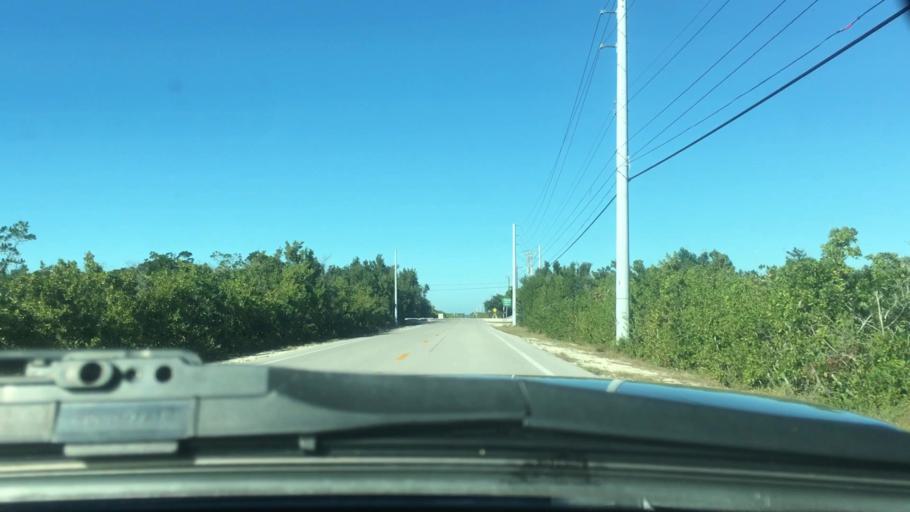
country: US
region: Florida
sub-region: Monroe County
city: Cudjoe Key
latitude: 24.6762
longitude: -81.4996
